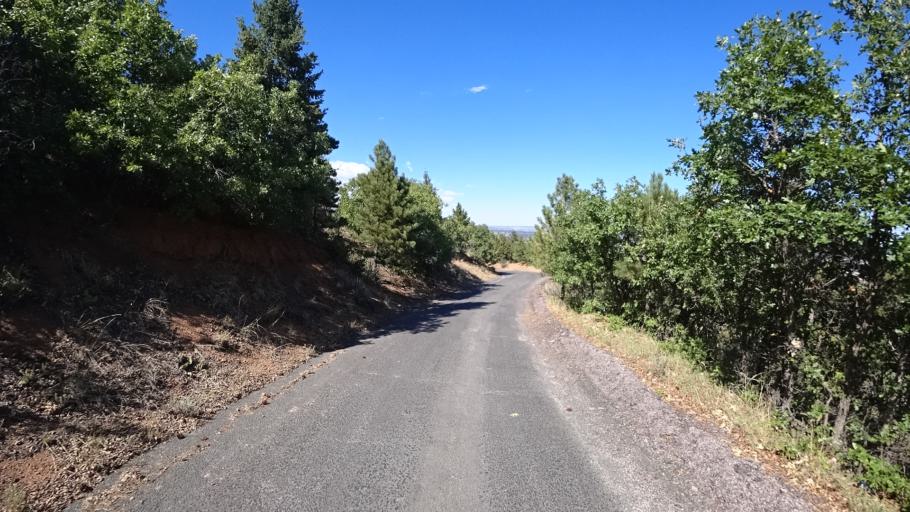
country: US
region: Colorado
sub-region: El Paso County
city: Colorado Springs
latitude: 38.8097
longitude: -104.8753
